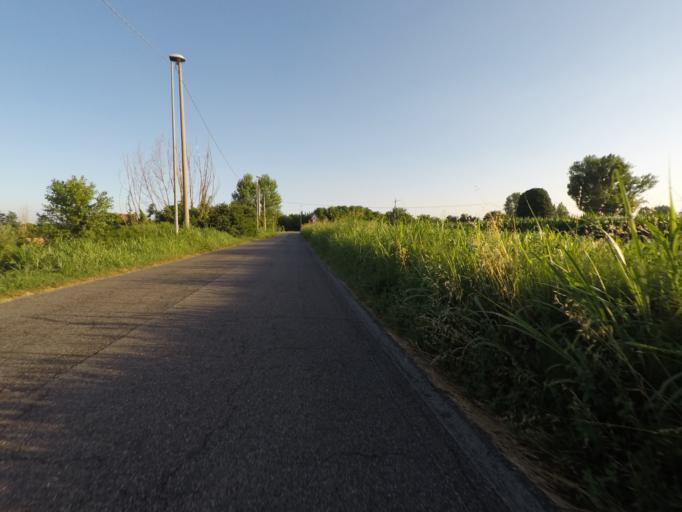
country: IT
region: Veneto
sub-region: Provincia di Rovigo
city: Fratta Polesine
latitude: 45.0394
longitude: 11.6463
